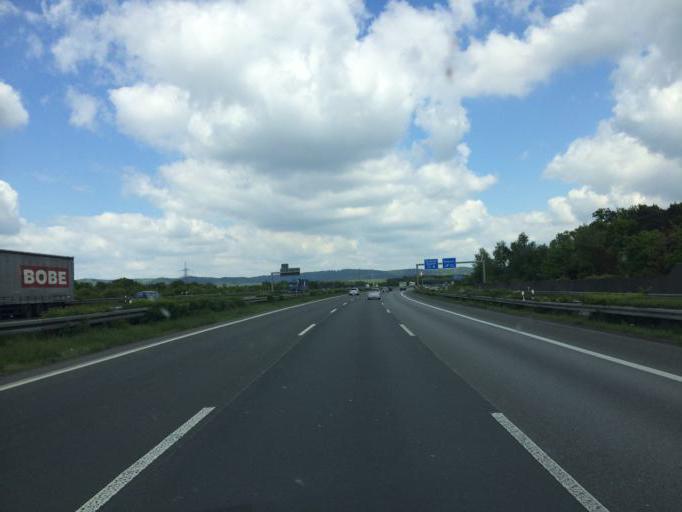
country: DE
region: North Rhine-Westphalia
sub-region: Regierungsbezirk Detmold
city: Verl
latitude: 51.9405
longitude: 8.5390
